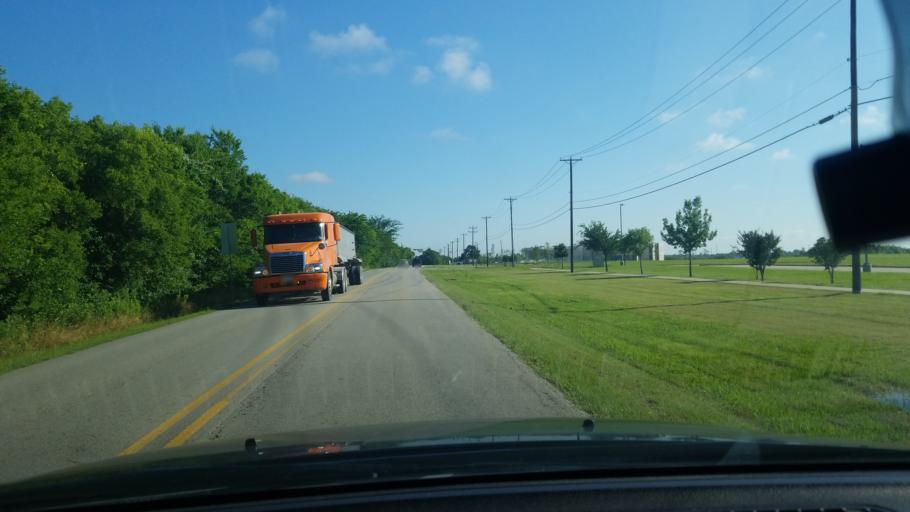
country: US
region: Texas
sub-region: Dallas County
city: Sunnyvale
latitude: 32.7990
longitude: -96.5610
